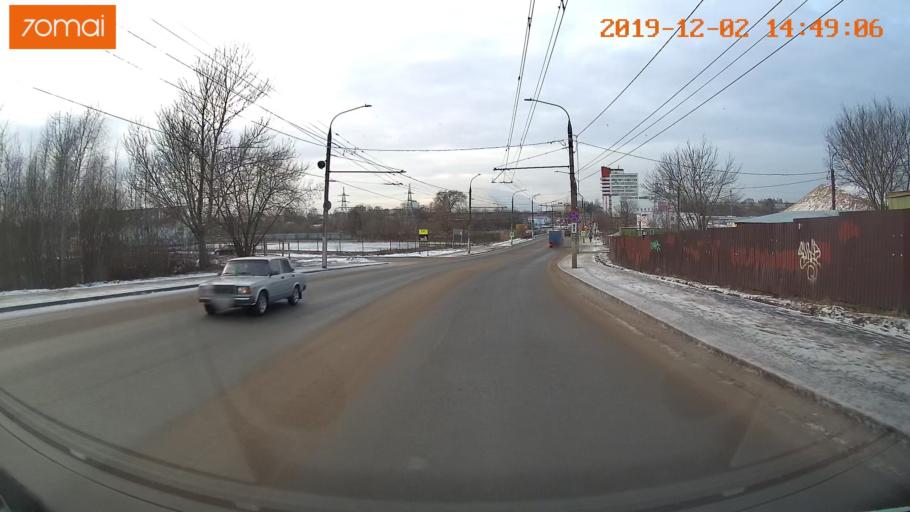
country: RU
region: Ivanovo
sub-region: Gorod Ivanovo
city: Ivanovo
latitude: 56.9841
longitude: 41.0135
